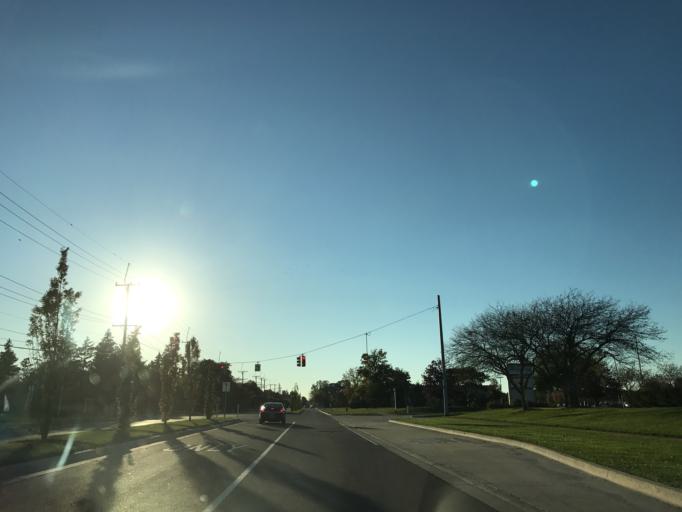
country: US
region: Michigan
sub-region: Oakland County
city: Franklin
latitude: 42.4857
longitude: -83.3135
